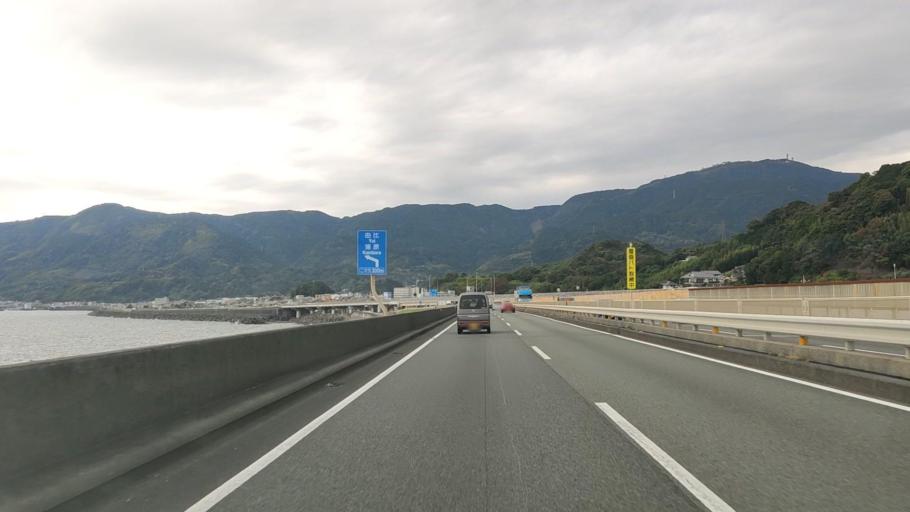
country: JP
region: Shizuoka
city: Fujinomiya
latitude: 35.1127
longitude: 138.5806
